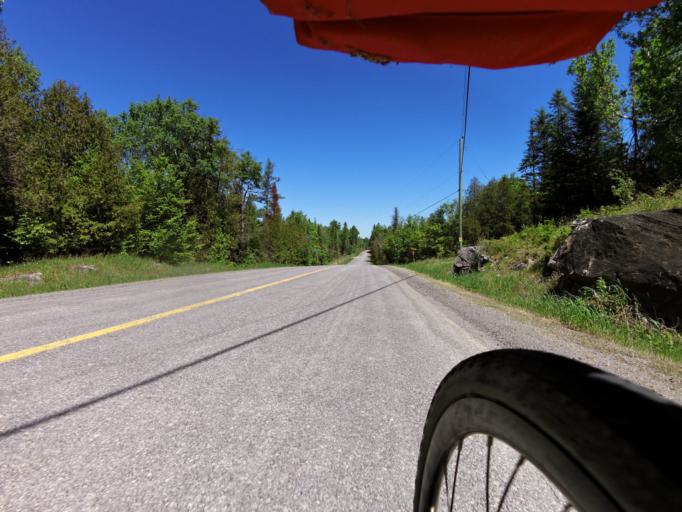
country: CA
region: Ontario
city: Carleton Place
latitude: 45.1766
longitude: -76.4059
